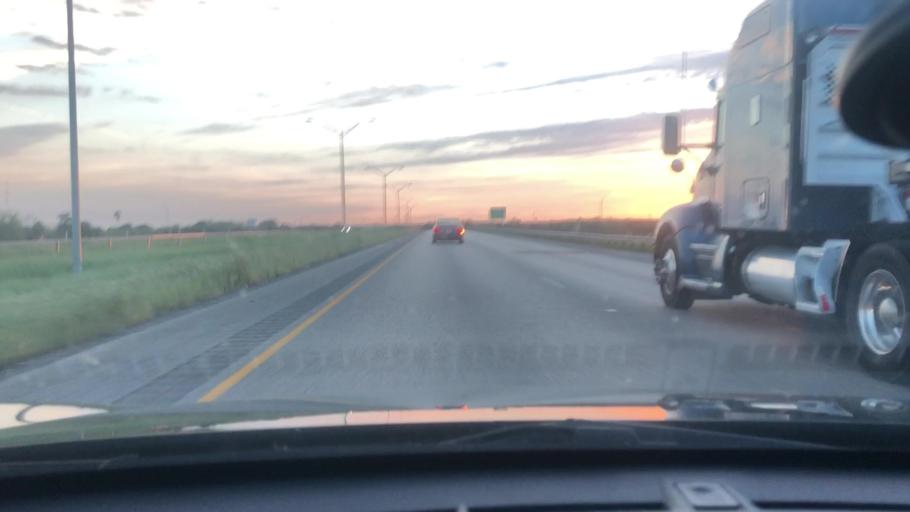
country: US
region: Texas
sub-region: Jackson County
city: Edna
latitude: 28.9845
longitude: -96.6558
